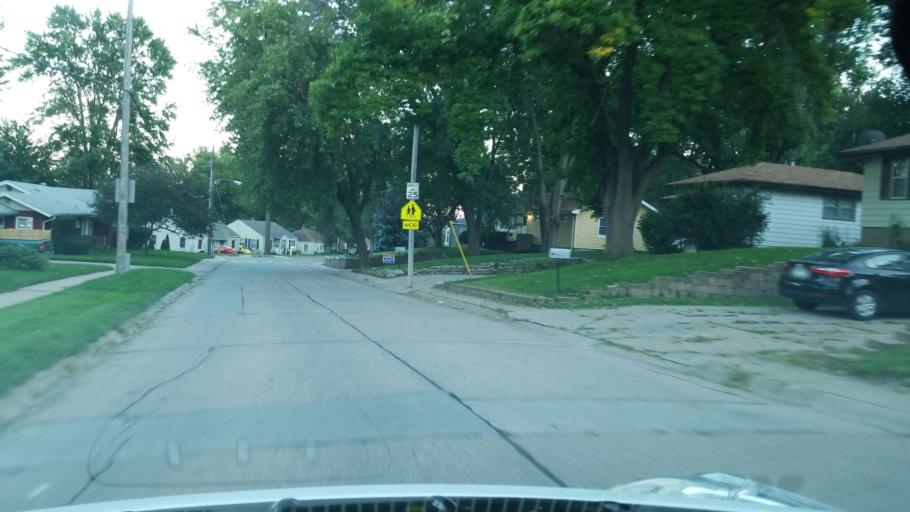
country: US
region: Nebraska
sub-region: Sarpy County
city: Bellevue
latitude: 41.1402
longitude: -95.9008
